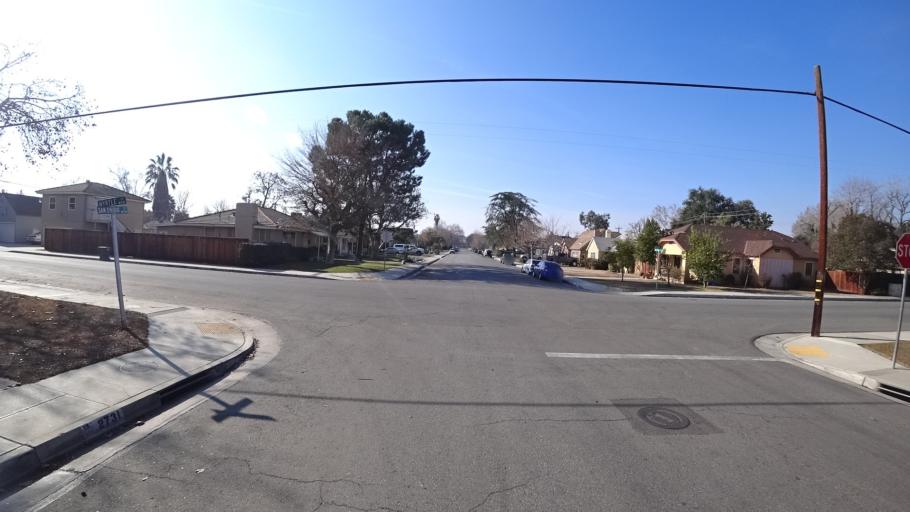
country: US
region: California
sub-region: Kern County
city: Bakersfield
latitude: 35.3658
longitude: -119.0340
